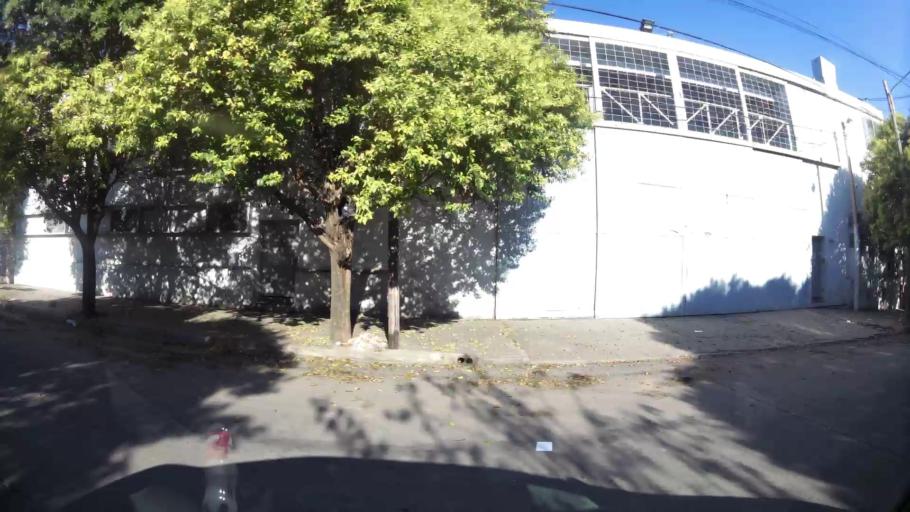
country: AR
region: Cordoba
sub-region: Departamento de Capital
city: Cordoba
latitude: -31.3919
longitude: -64.1770
